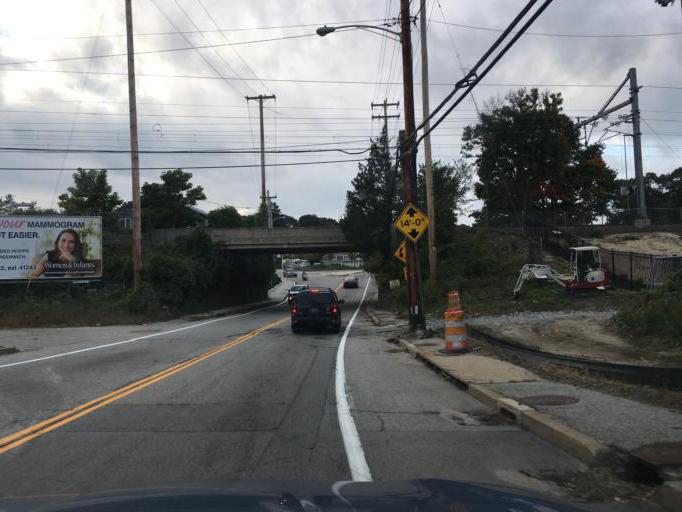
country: US
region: Rhode Island
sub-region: Kent County
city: Warwick
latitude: 41.6991
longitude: -71.4516
